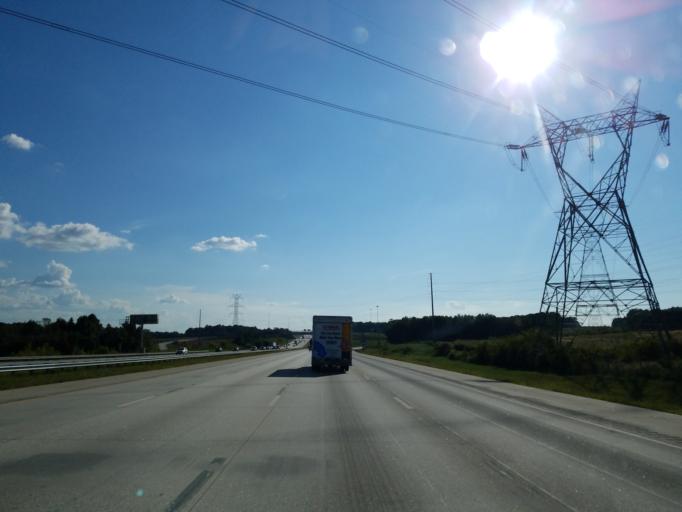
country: US
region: North Carolina
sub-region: Davidson County
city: Tyro
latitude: 35.7370
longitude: -80.3689
